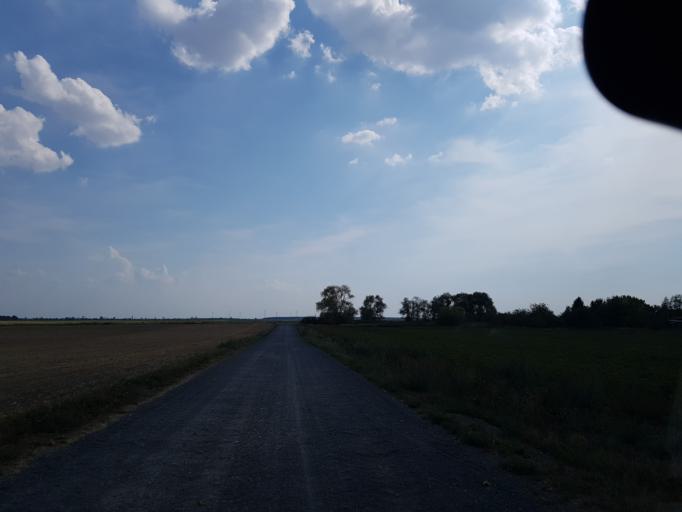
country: DE
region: Brandenburg
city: Treuenbrietzen
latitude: 51.9921
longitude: 12.8686
